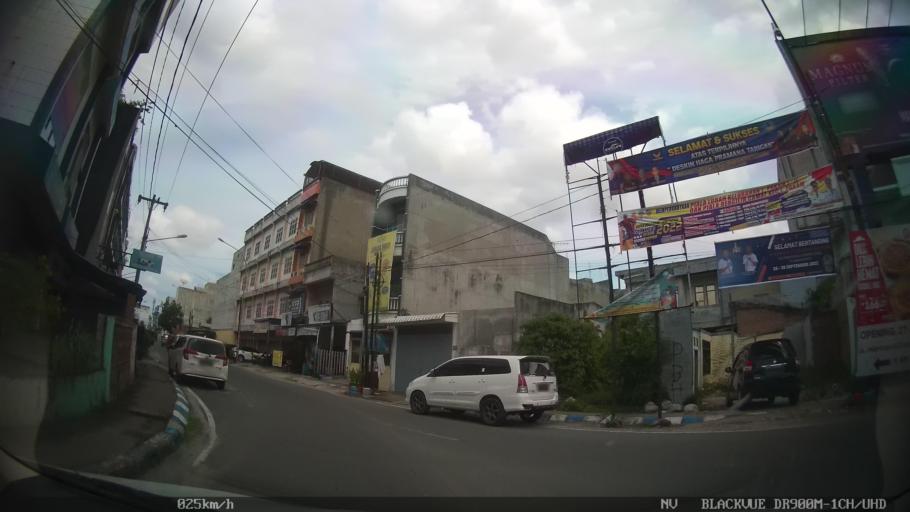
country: ID
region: North Sumatra
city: Percut
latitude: 3.5634
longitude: 98.8740
